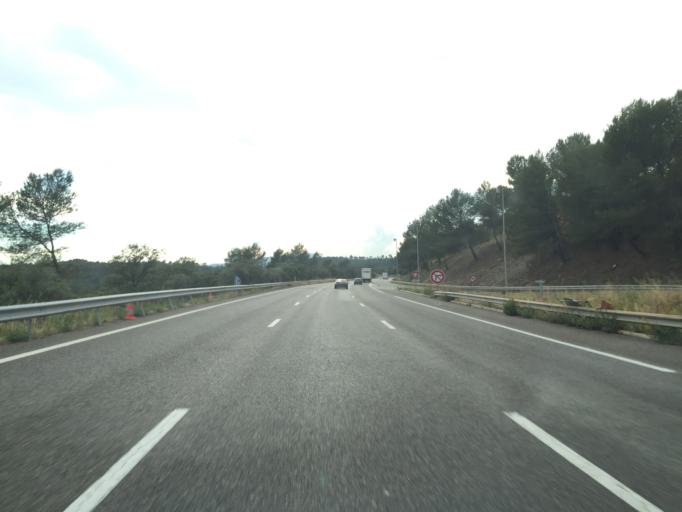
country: FR
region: Provence-Alpes-Cote d'Azur
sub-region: Departement du Var
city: La Celle
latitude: 43.4233
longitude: 5.9890
